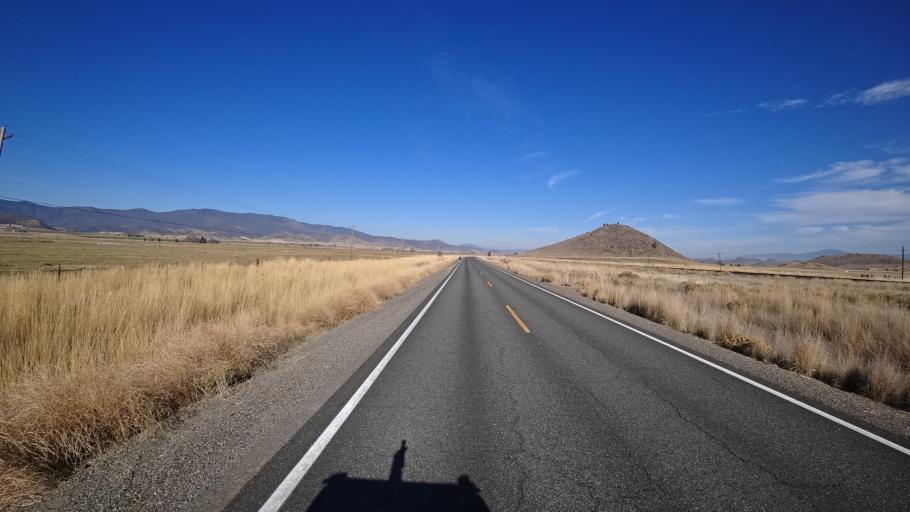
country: US
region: California
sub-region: Siskiyou County
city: Weed
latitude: 41.5276
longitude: -122.5224
